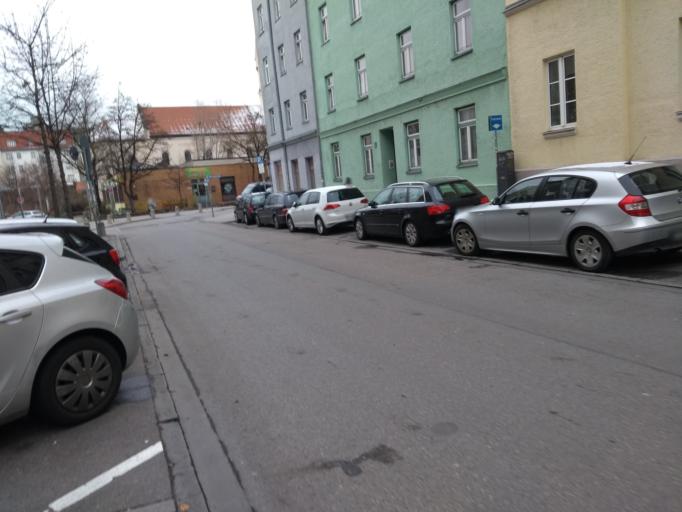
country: DE
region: Bavaria
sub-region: Upper Bavaria
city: Munich
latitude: 48.1377
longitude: 11.5407
